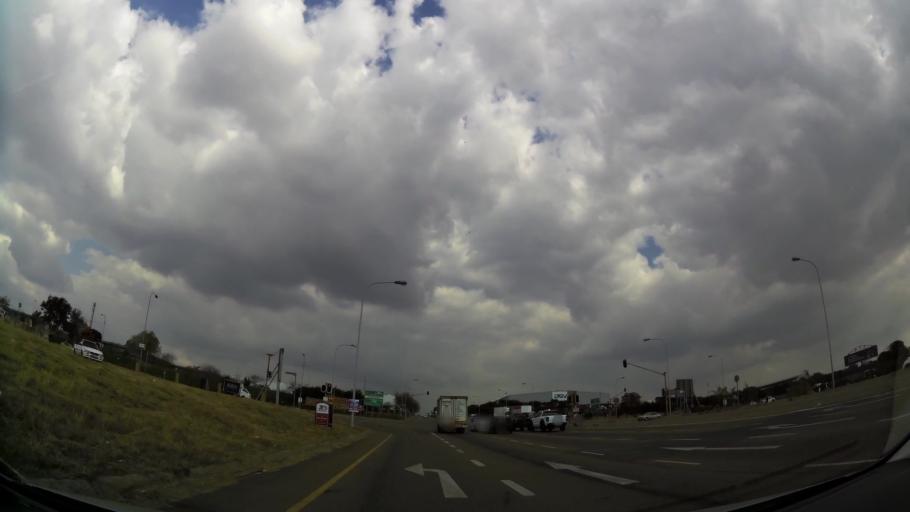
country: ZA
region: Gauteng
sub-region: City of Tshwane Metropolitan Municipality
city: Centurion
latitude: -25.9098
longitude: 28.1653
